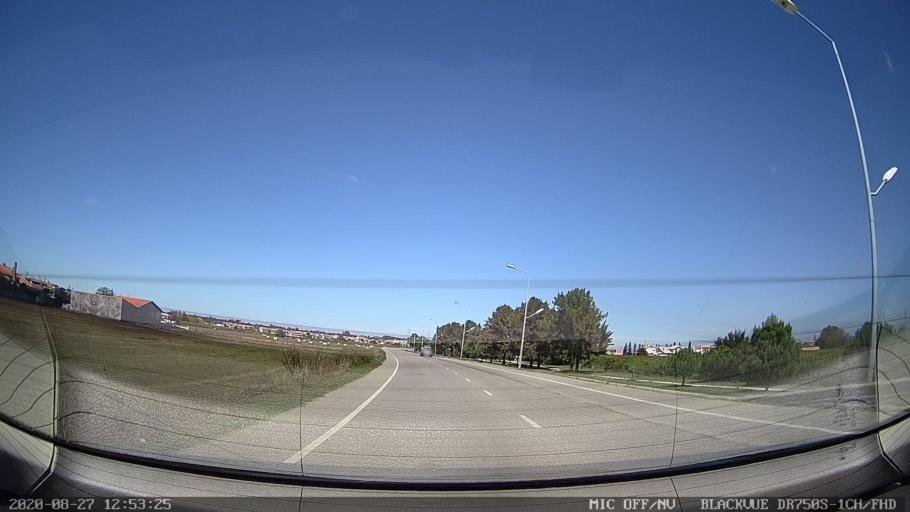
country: PT
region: Aveiro
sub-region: Ilhavo
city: Ilhavo
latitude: 40.6001
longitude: -8.6780
